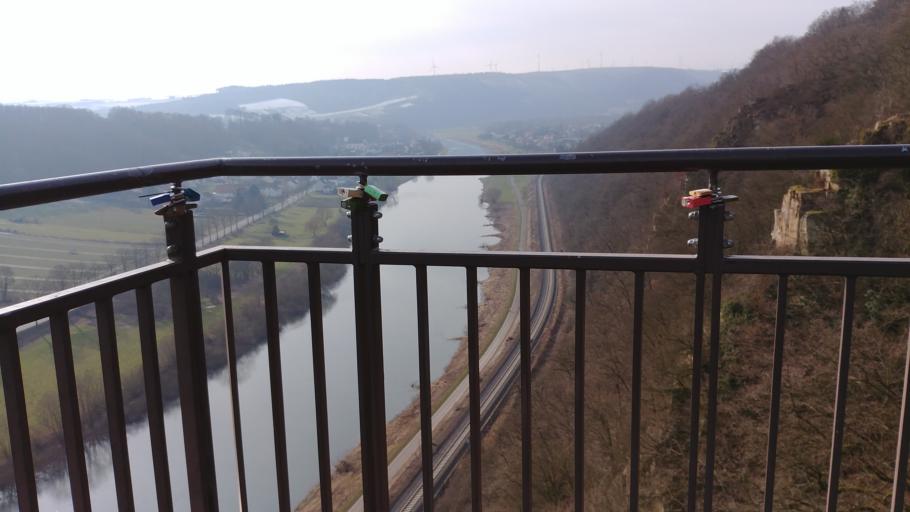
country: DE
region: Lower Saxony
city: Bad Karlshafen
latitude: 51.6499
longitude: 9.4333
